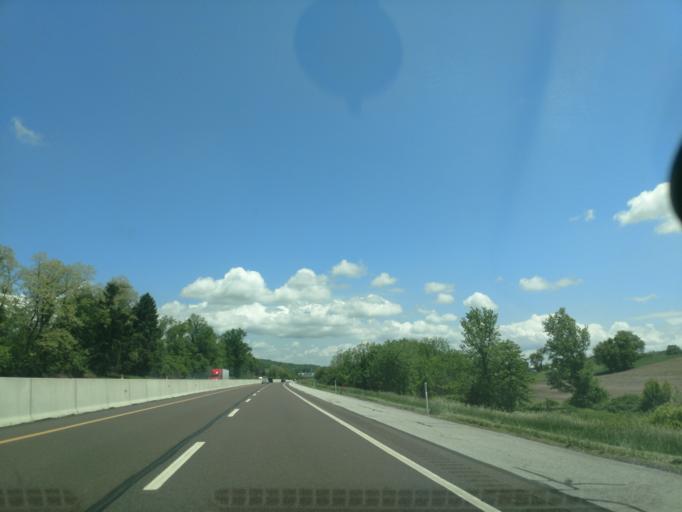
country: US
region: Pennsylvania
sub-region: Lancaster County
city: Clay
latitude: 40.2455
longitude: -76.2222
